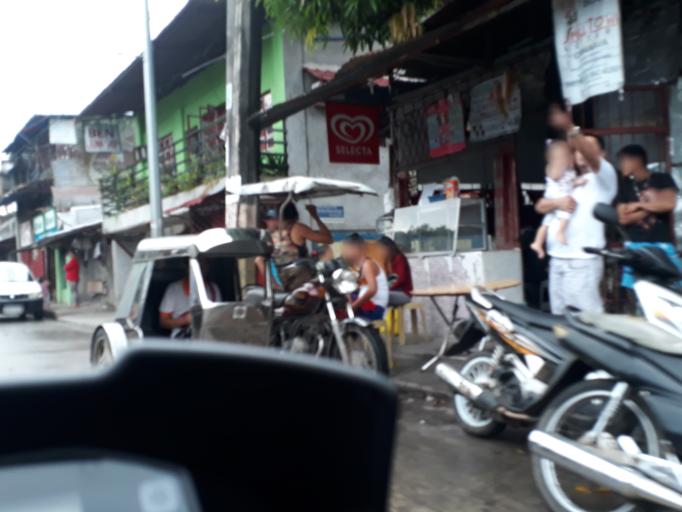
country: PH
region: Central Luzon
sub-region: Province of Bulacan
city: San Jose del Monte
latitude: 14.7707
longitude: 121.0519
